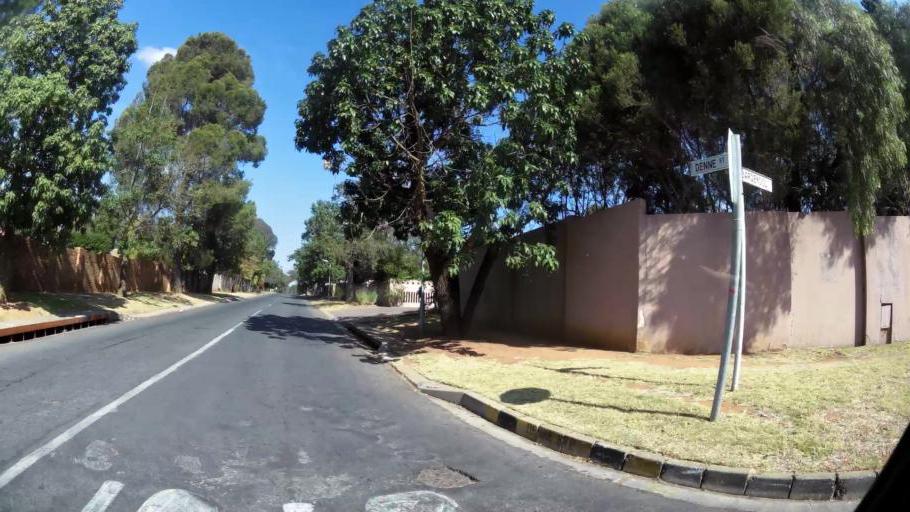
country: ZA
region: Gauteng
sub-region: City of Johannesburg Metropolitan Municipality
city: Roodepoort
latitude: -26.0785
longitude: 27.9407
